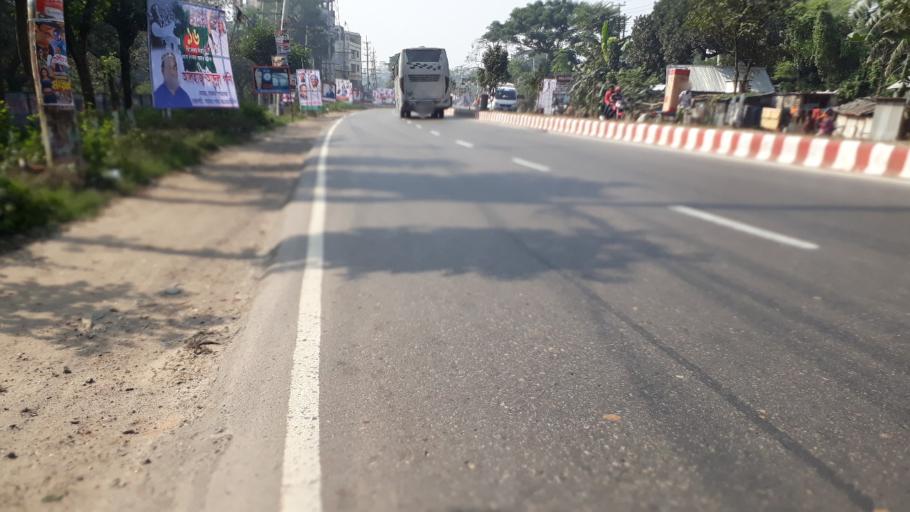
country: BD
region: Dhaka
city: Tungi
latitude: 23.8617
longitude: 90.2659
